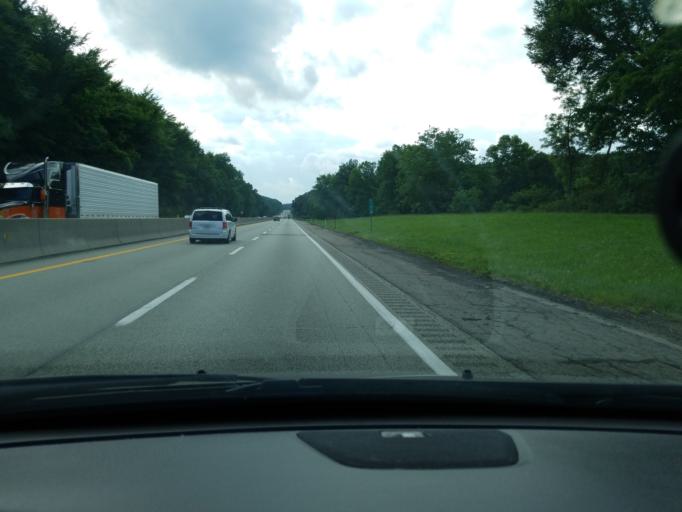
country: US
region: Pennsylvania
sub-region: Lawrence County
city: Ellport
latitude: 40.7859
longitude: -80.2467
